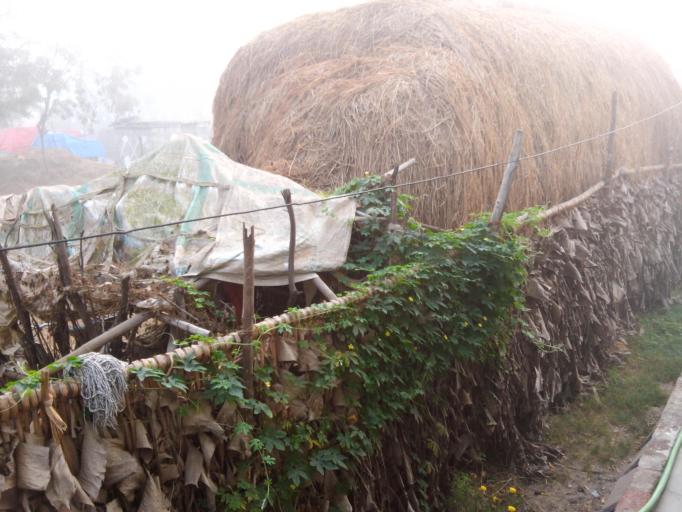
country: IN
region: Andhra Pradesh
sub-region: Krishna
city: Yanamalakuduru
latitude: 16.4310
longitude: 80.6548
